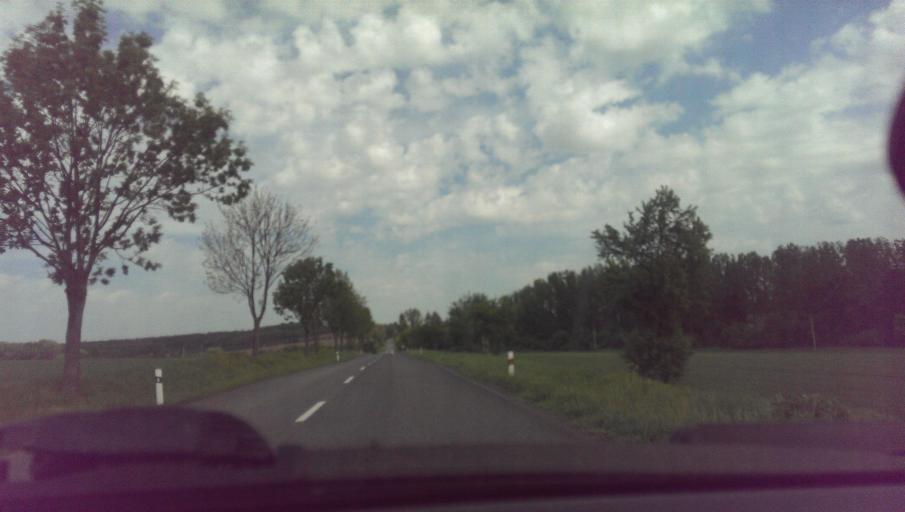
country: CZ
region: Zlin
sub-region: Okres Zlin
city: Otrokovice
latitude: 49.2275
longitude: 17.5361
